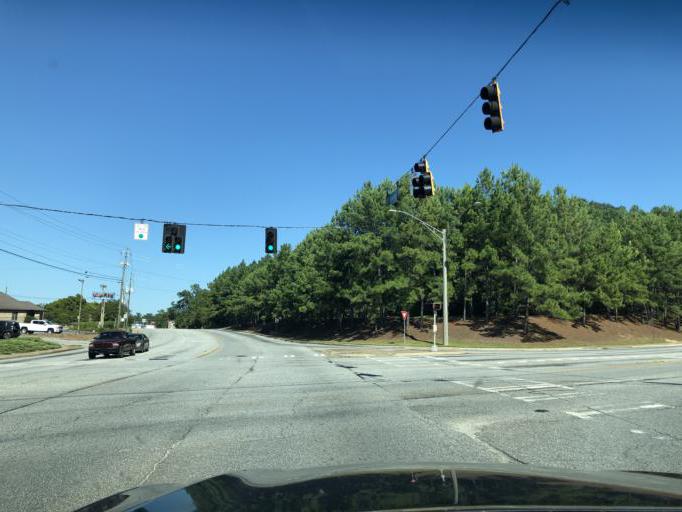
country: US
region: Georgia
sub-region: Muscogee County
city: Columbus
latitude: 32.5055
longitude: -84.9397
